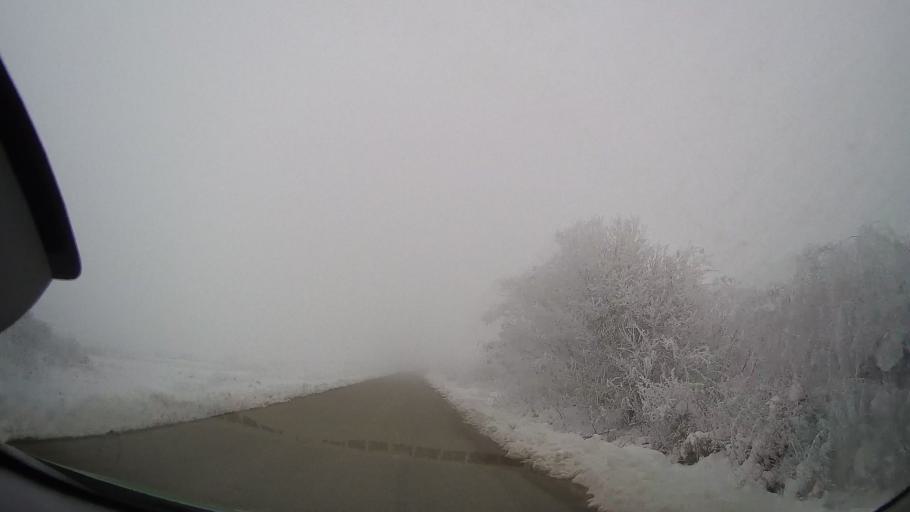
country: RO
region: Iasi
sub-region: Comuna Tansa
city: Suhulet
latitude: 46.8901
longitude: 27.2692
